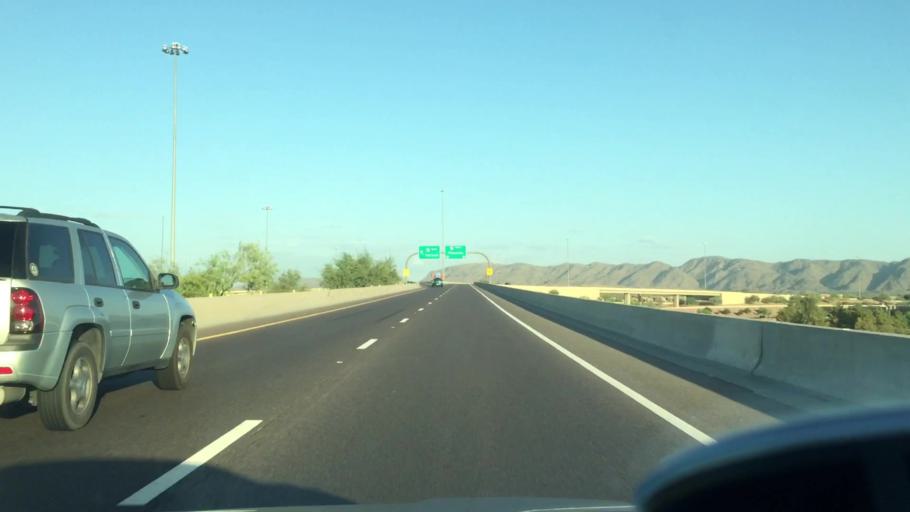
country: US
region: Arizona
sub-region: Maricopa County
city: Guadalupe
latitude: 33.2967
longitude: -111.9657
